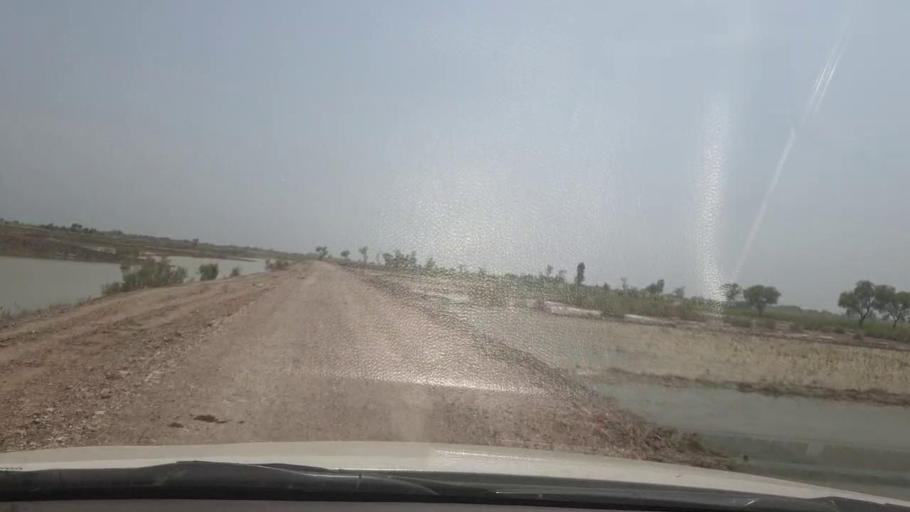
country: PK
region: Sindh
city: Shikarpur
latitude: 28.0339
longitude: 68.5736
